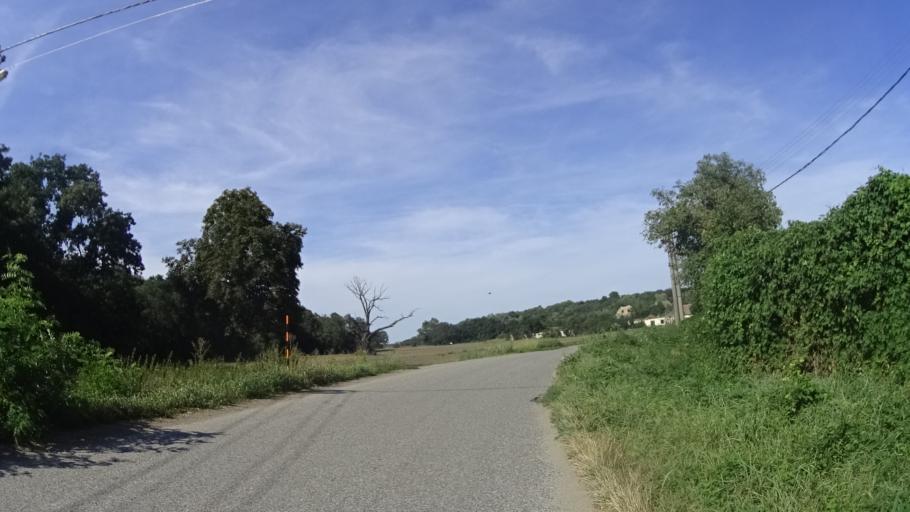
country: AT
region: Lower Austria
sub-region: Politischer Bezirk Ganserndorf
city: Angern an der March
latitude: 48.4147
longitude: 16.8735
